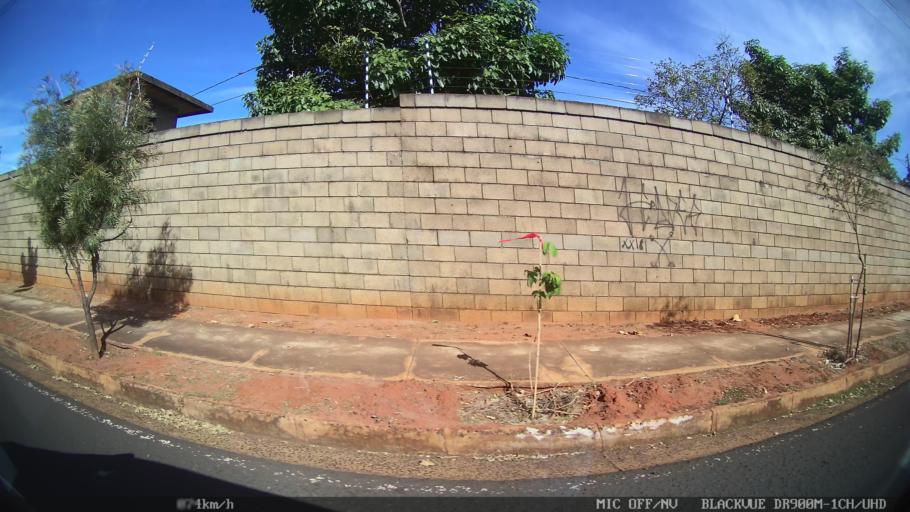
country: BR
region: Sao Paulo
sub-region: Sao Jose Do Rio Preto
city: Sao Jose do Rio Preto
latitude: -20.8008
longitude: -49.3390
